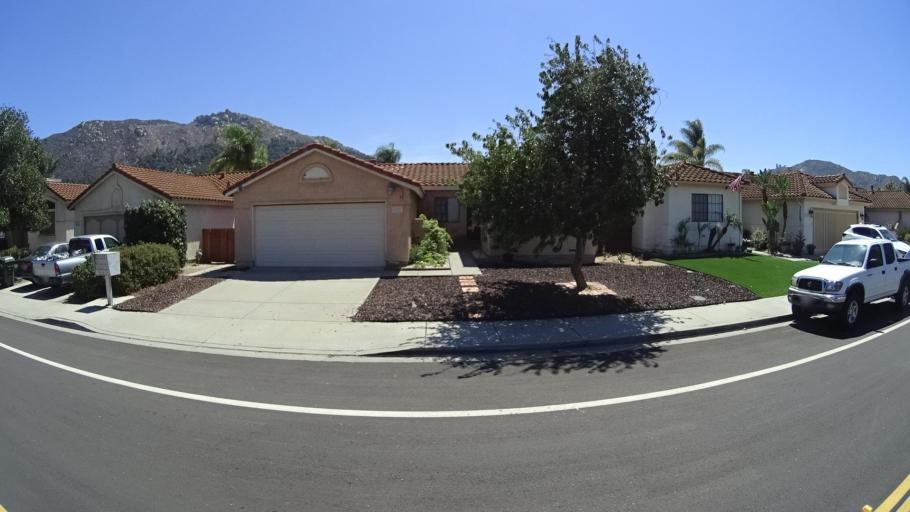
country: US
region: California
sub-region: San Diego County
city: Bonsall
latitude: 33.3264
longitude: -117.1533
